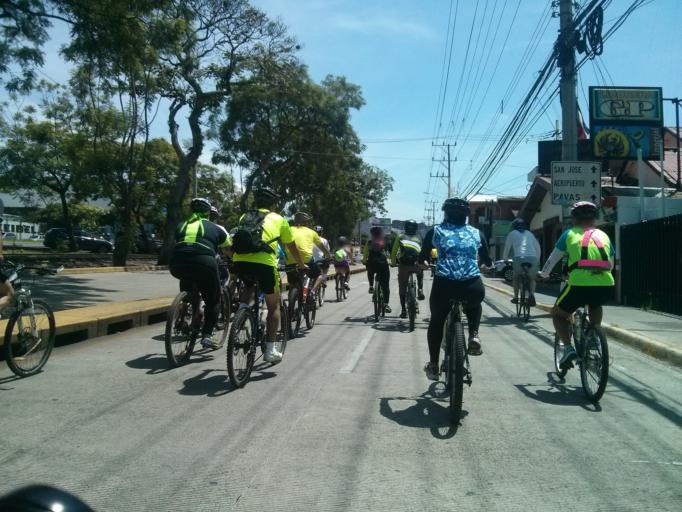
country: CR
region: San Jose
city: San Jose
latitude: 9.9323
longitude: -84.1001
